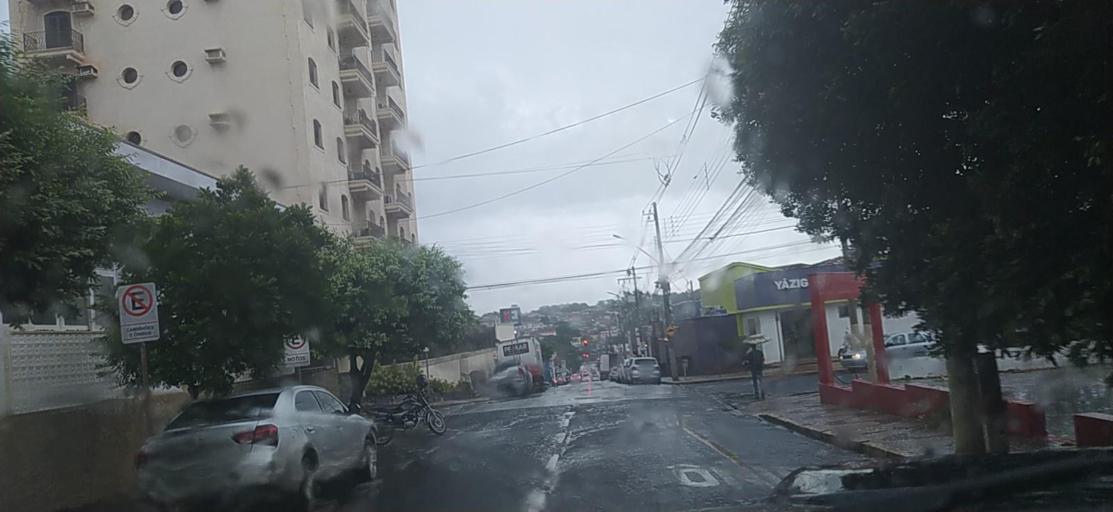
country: BR
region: Sao Paulo
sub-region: Catanduva
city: Catanduva
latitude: -21.1369
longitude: -48.9707
